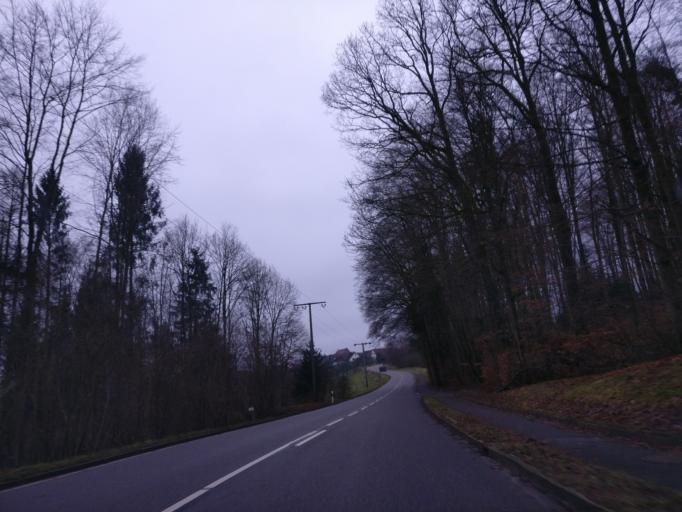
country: DE
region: Baden-Wuerttemberg
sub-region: Regierungsbezirk Stuttgart
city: Rudersberg
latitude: 48.8586
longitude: 9.4993
